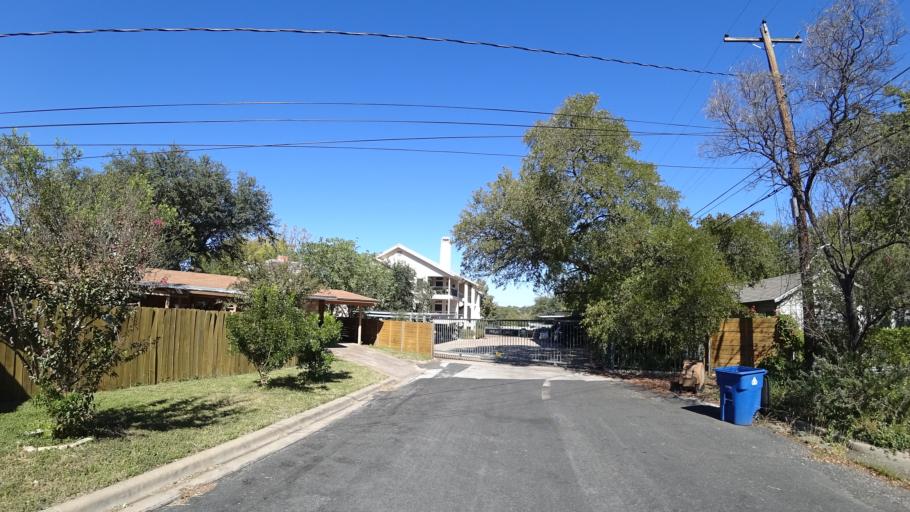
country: US
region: Texas
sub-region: Travis County
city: Austin
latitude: 30.3213
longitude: -97.7411
